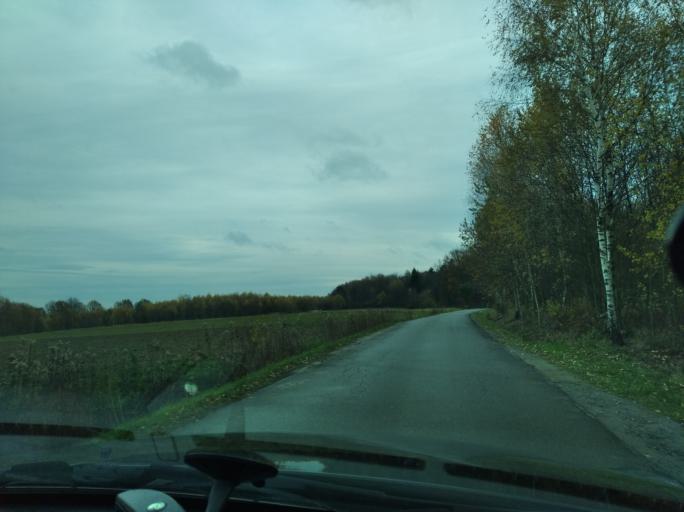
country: PL
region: Subcarpathian Voivodeship
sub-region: Powiat strzyzowski
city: Strzyzow
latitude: 49.9105
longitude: 21.7736
